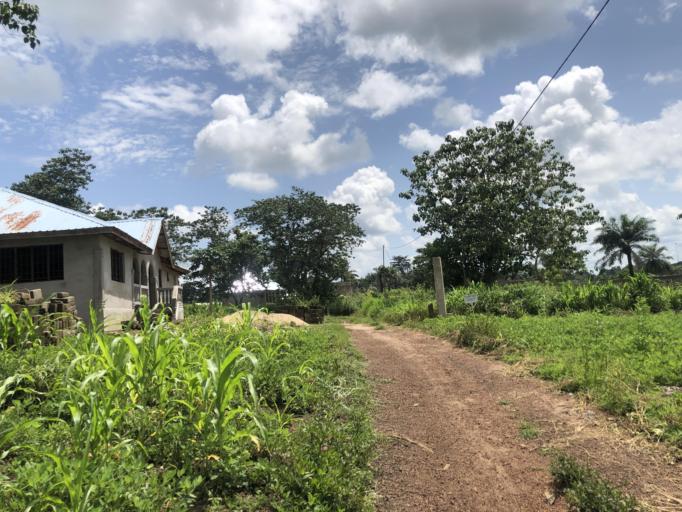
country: SL
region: Northern Province
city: Magburaka
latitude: 8.7113
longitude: -11.9283
